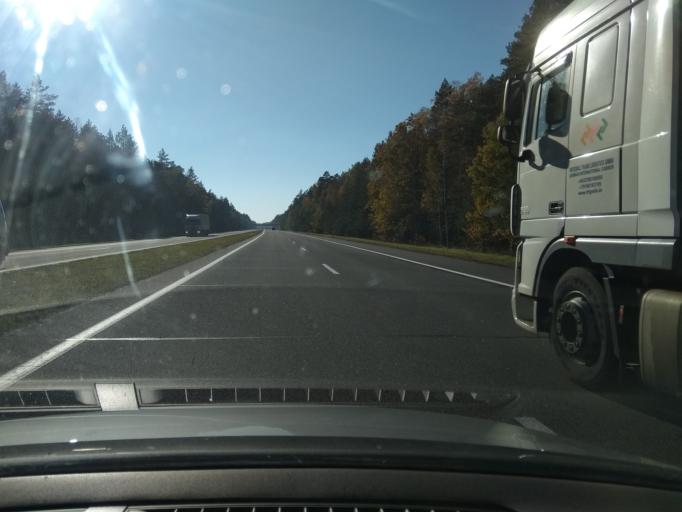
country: BY
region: Brest
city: Baranovichi
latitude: 53.0396
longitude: 25.8236
